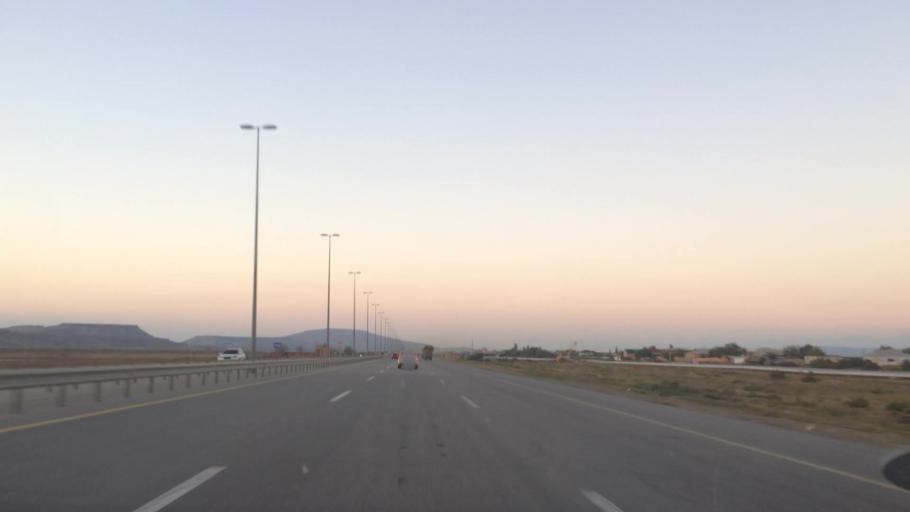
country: AZ
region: Baki
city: Qobustan
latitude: 40.0136
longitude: 49.4267
